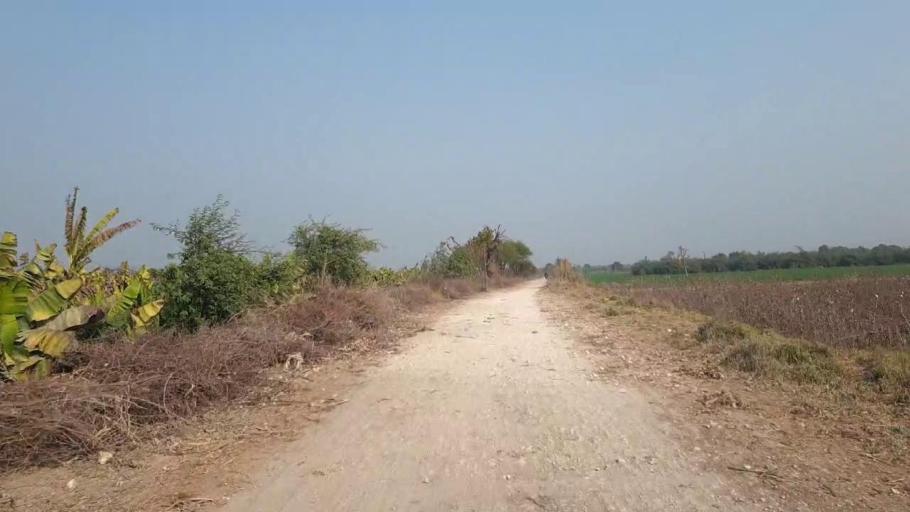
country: PK
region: Sindh
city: Bhit Shah
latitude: 25.8835
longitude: 68.4685
